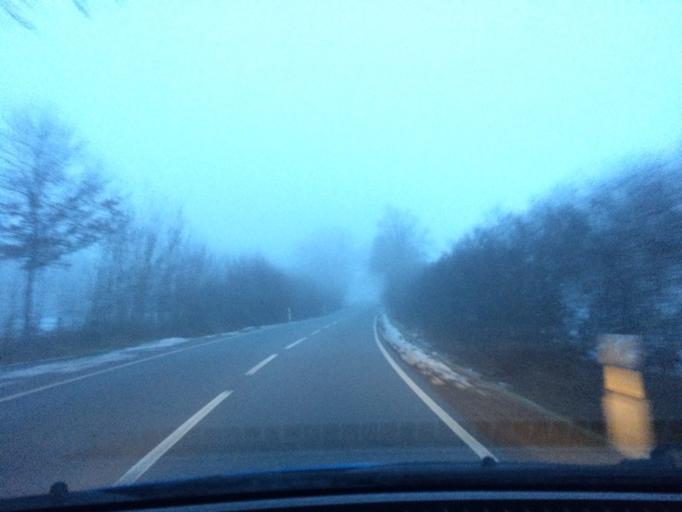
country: DE
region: Schleswig-Holstein
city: Kollow
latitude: 53.4824
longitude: 10.4659
